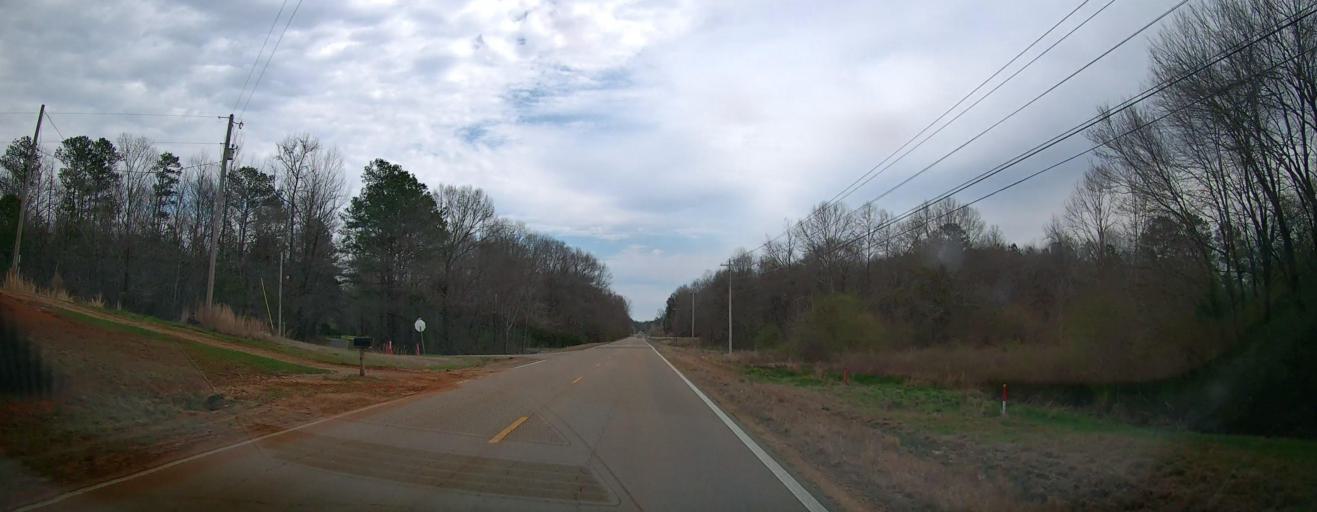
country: US
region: Mississippi
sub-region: Itawamba County
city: Fulton
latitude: 34.2582
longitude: -88.3178
